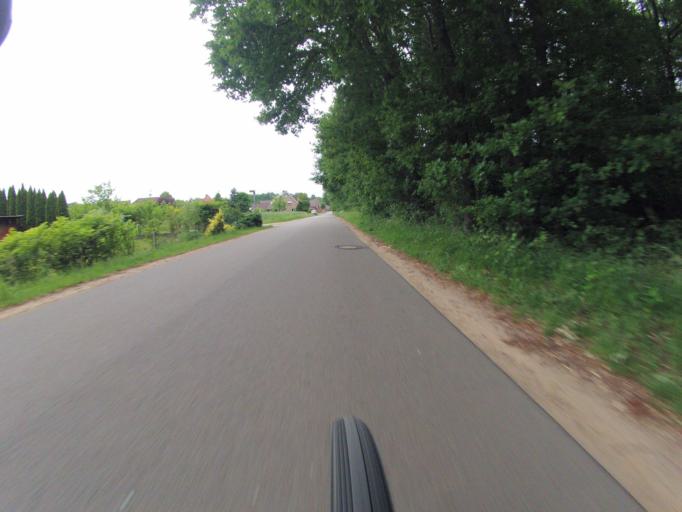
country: DE
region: North Rhine-Westphalia
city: Emsdetten
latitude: 52.2331
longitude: 7.5154
